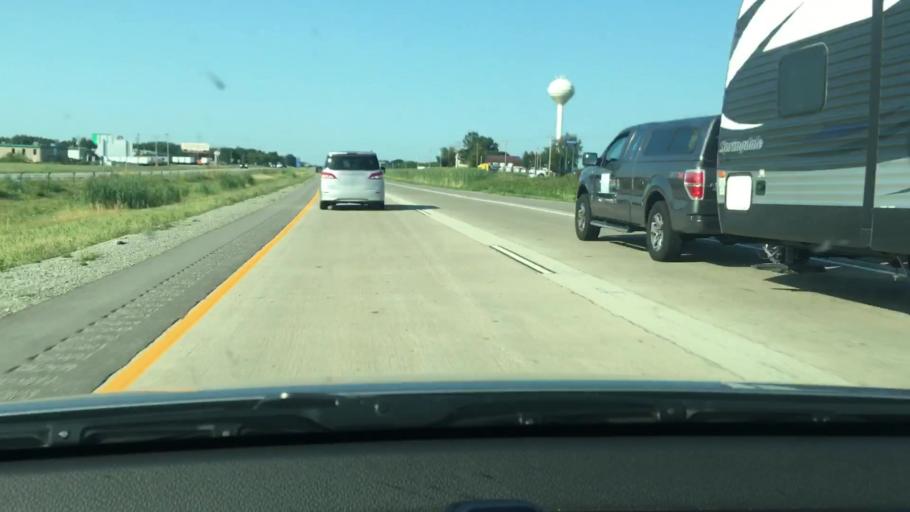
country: US
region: Wisconsin
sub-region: Brown County
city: De Pere
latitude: 44.4195
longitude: -88.1296
